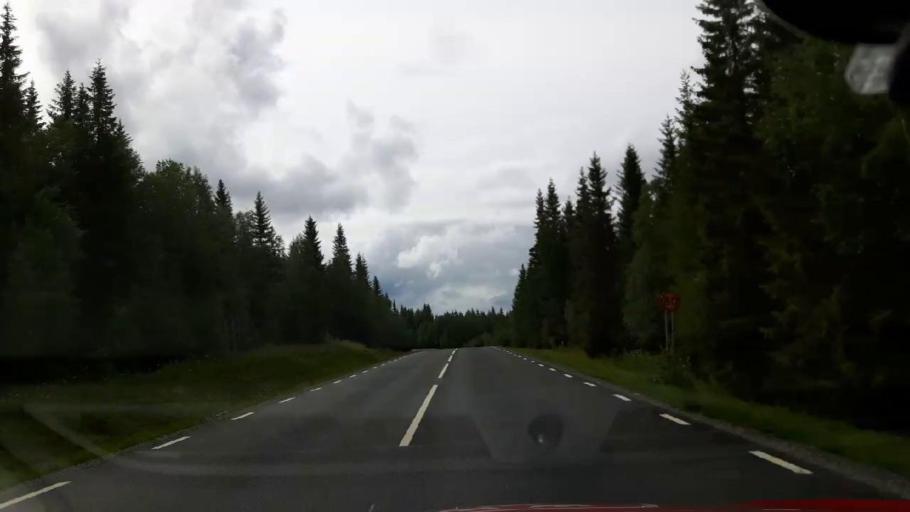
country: NO
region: Nord-Trondelag
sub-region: Lierne
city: Sandvika
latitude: 64.6413
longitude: 14.1387
